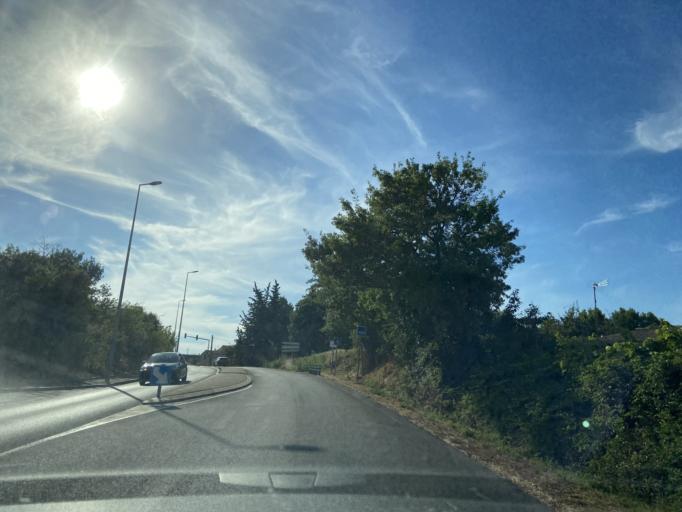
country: FR
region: Provence-Alpes-Cote d'Azur
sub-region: Departement des Bouches-du-Rhone
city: Miramas
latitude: 43.5782
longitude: 5.0107
